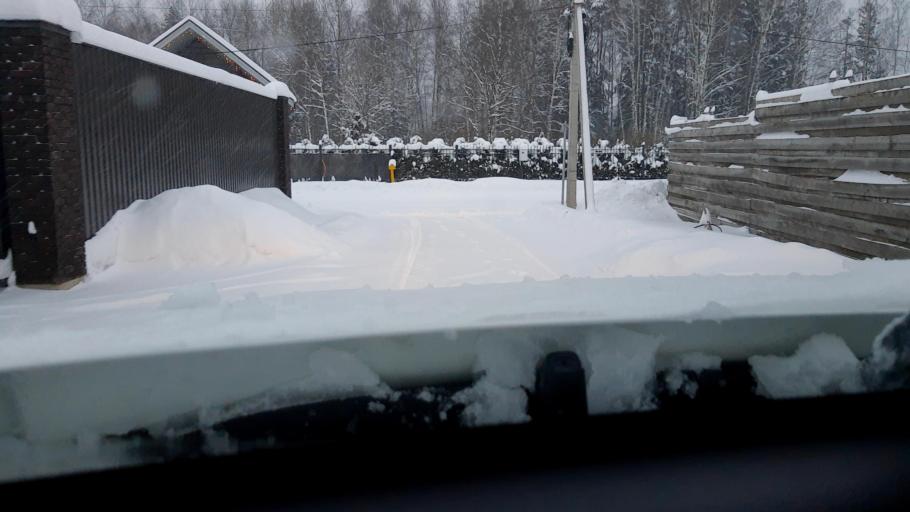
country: RU
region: Moskovskaya
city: Firsanovka
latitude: 55.9072
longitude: 37.2006
